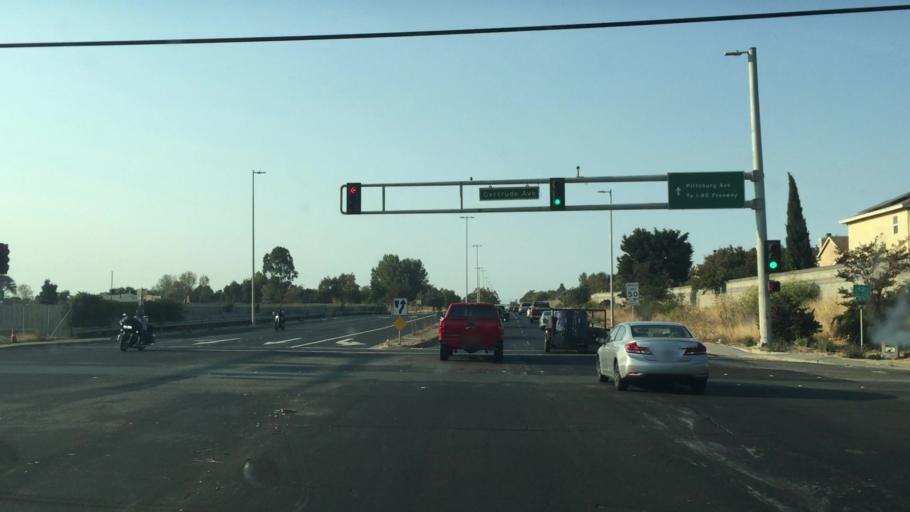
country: US
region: California
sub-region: Contra Costa County
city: North Richmond
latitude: 37.9539
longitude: -122.3736
